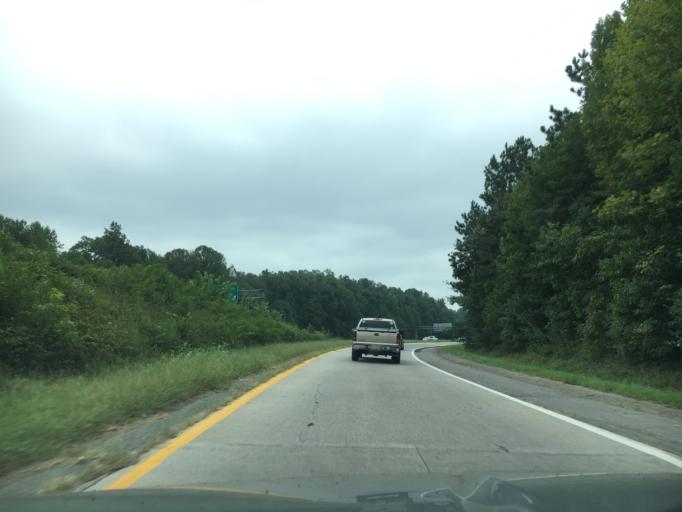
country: US
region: Virginia
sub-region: Chesterfield County
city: Brandermill
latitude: 37.4219
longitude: -77.6302
